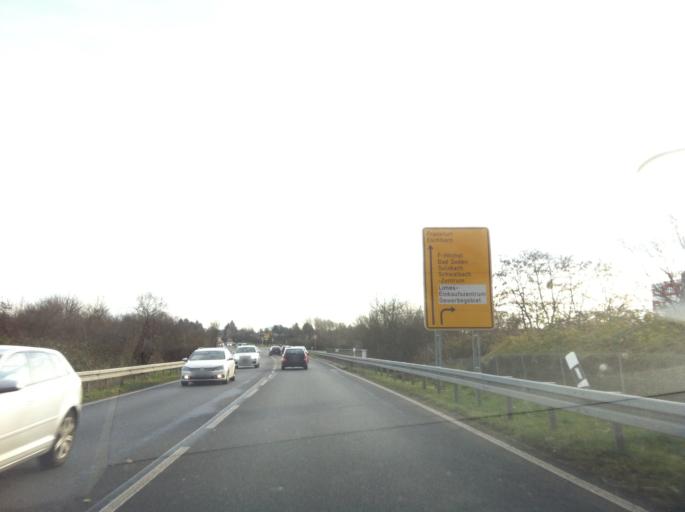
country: DE
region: Hesse
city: Schwalbach am Taunus
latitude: 50.1606
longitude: 8.5369
